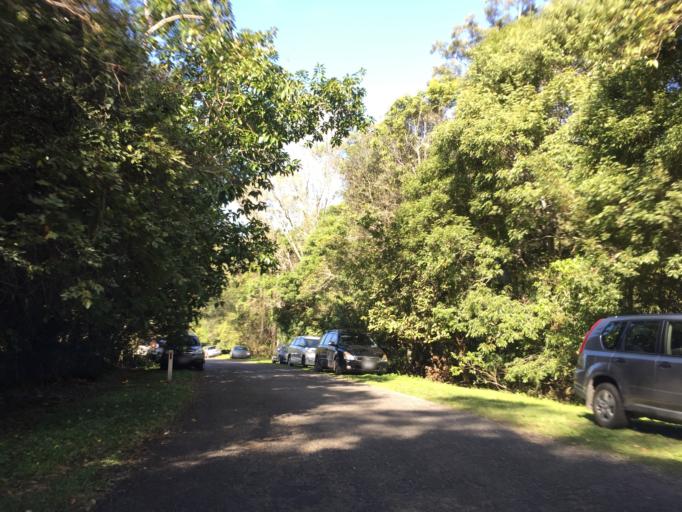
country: AU
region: Queensland
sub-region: Brisbane
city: Pullenvale
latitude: -27.4643
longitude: 152.8866
